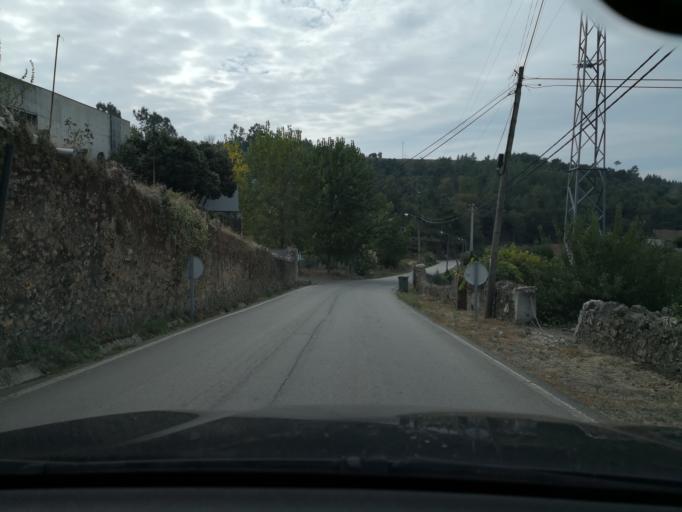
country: PT
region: Vila Real
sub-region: Peso da Regua
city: Peso da Regua
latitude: 41.1992
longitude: -7.7149
